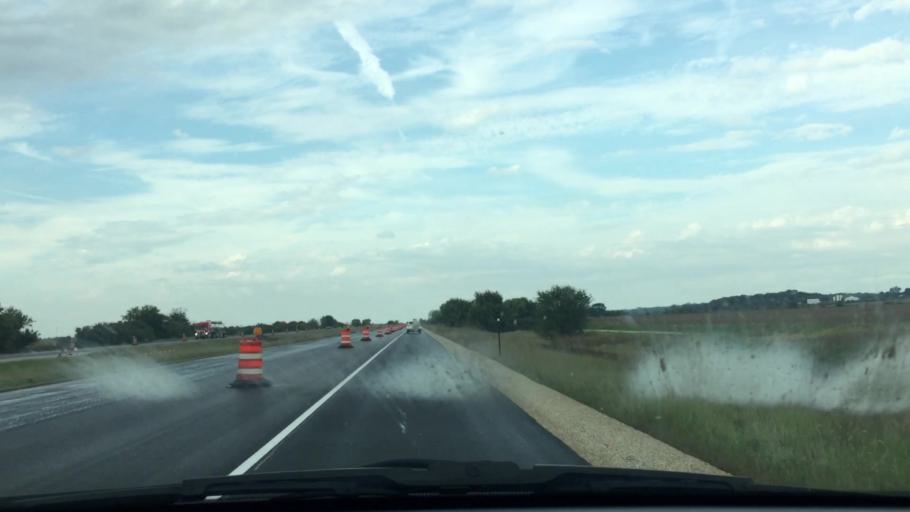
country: US
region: Illinois
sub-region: Whiteside County
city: Erie
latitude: 41.7111
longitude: -90.0135
